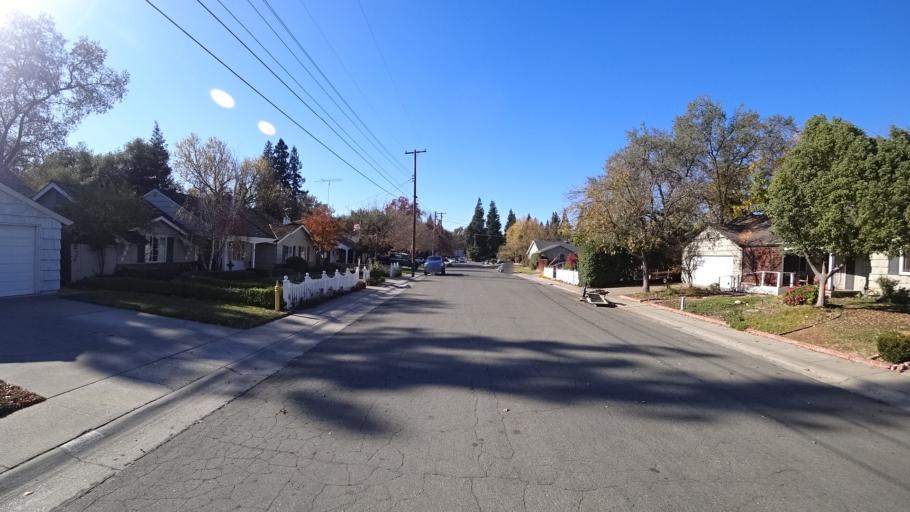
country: US
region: California
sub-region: Sacramento County
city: Foothill Farms
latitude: 38.6747
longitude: -121.3181
